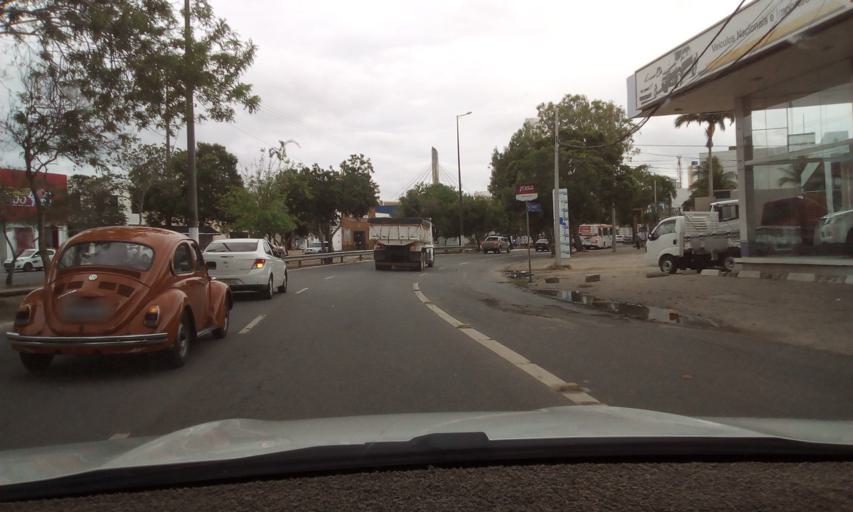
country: BR
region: Paraiba
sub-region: Campina Grande
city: Campina Grande
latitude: -7.2195
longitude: -35.8751
